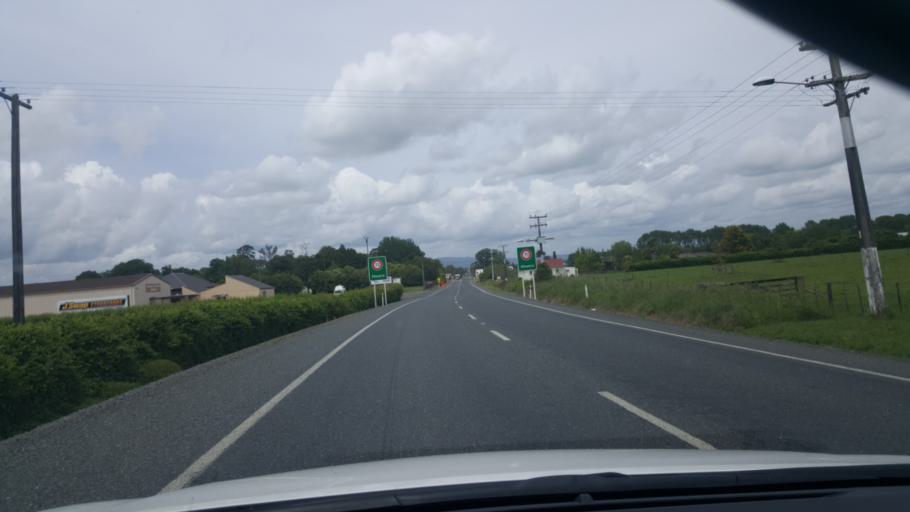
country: NZ
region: Waikato
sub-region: Matamata-Piako District
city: Matamata
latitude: -37.8794
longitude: 175.7546
